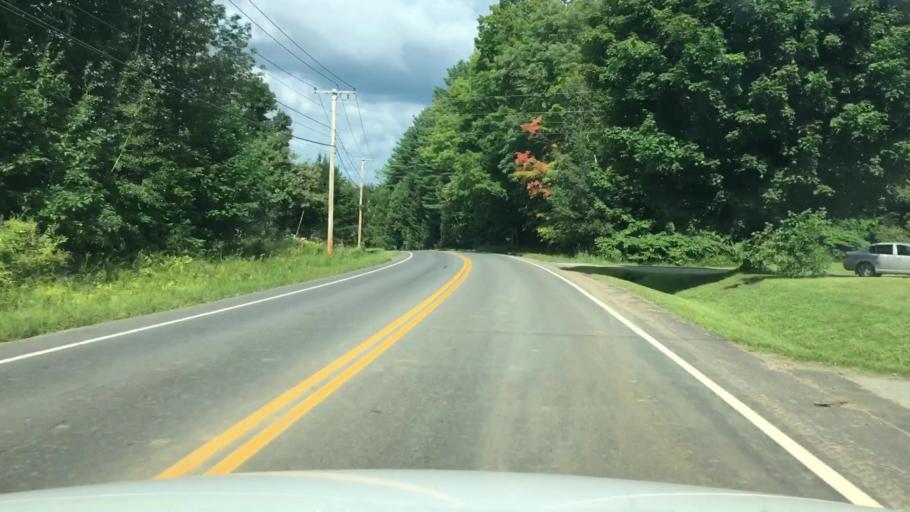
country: US
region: Maine
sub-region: Somerset County
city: Skowhegan
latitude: 44.7450
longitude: -69.6932
